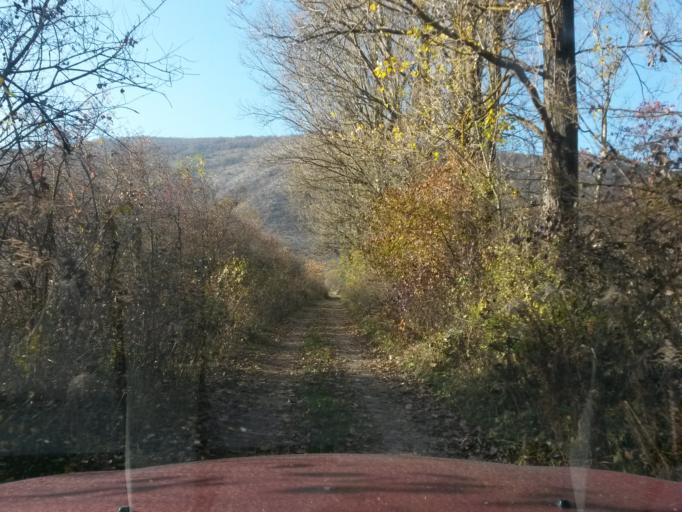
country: SK
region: Kosicky
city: Roznava
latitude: 48.5891
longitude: 20.4797
